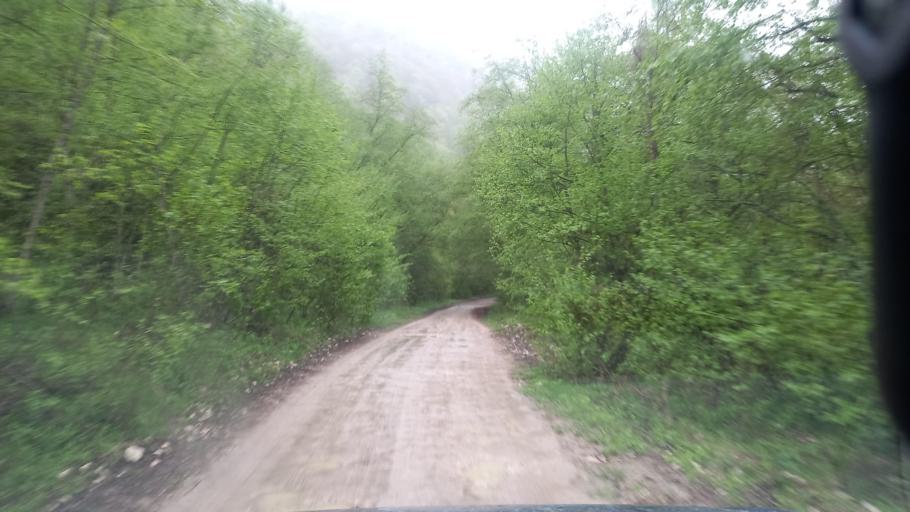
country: RU
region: Kabardino-Balkariya
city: Gundelen
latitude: 43.5790
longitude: 43.1016
